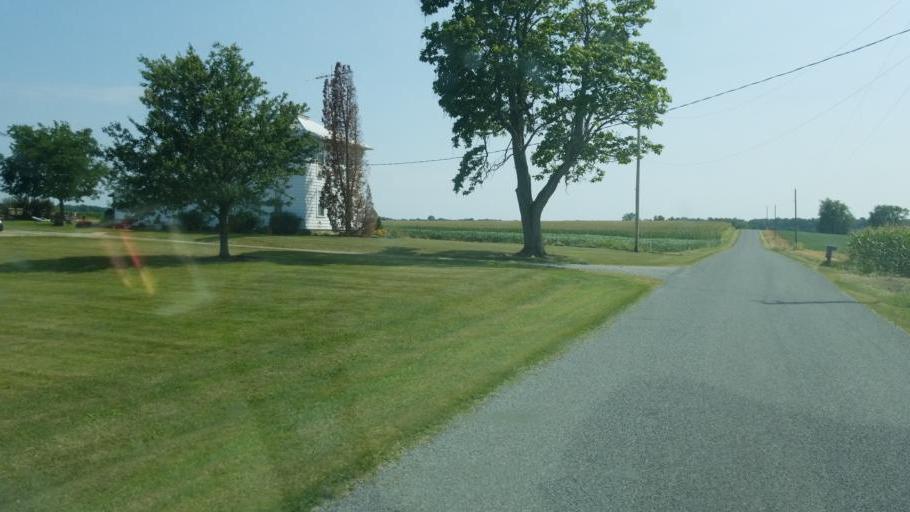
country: US
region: Ohio
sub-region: Crawford County
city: Crestline
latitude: 40.8984
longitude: -82.7982
